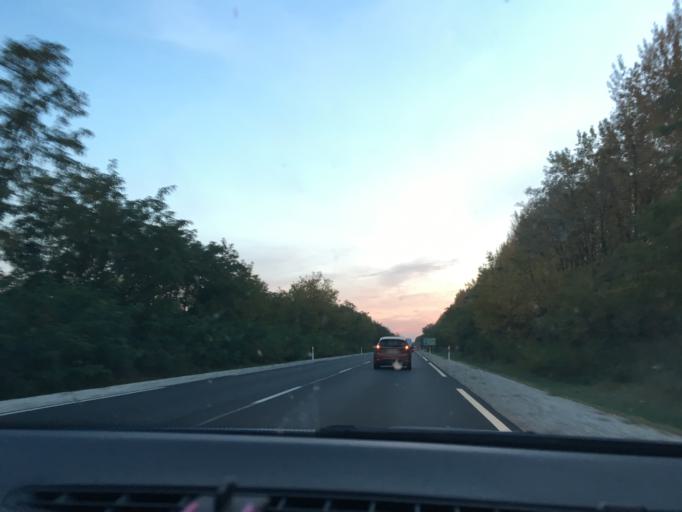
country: HU
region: Hajdu-Bihar
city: Hajduhadhaz
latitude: 47.6132
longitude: 21.6576
